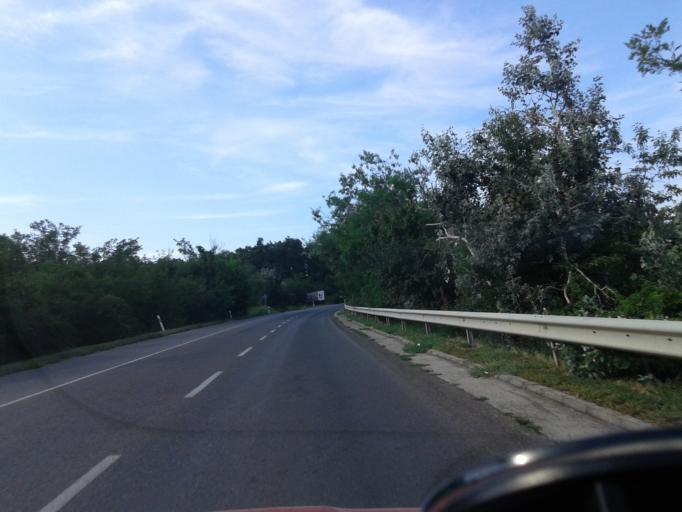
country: HU
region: Pest
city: Kerepes
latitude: 47.5777
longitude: 19.2915
